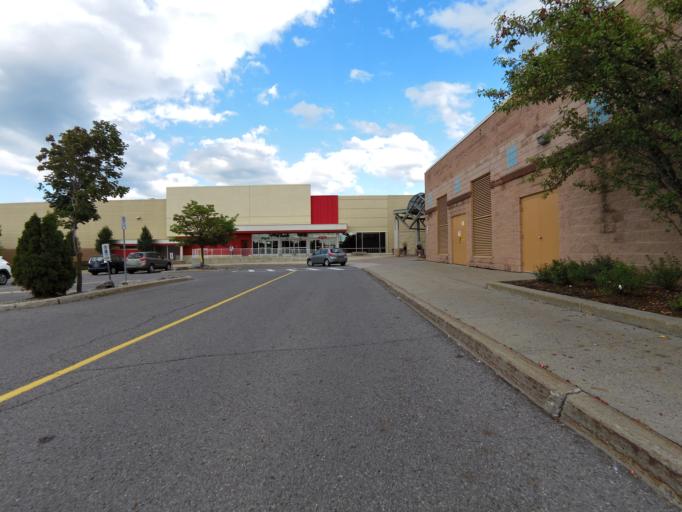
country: CA
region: Quebec
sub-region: Outaouais
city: Gatineau
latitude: 45.4791
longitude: -75.5153
